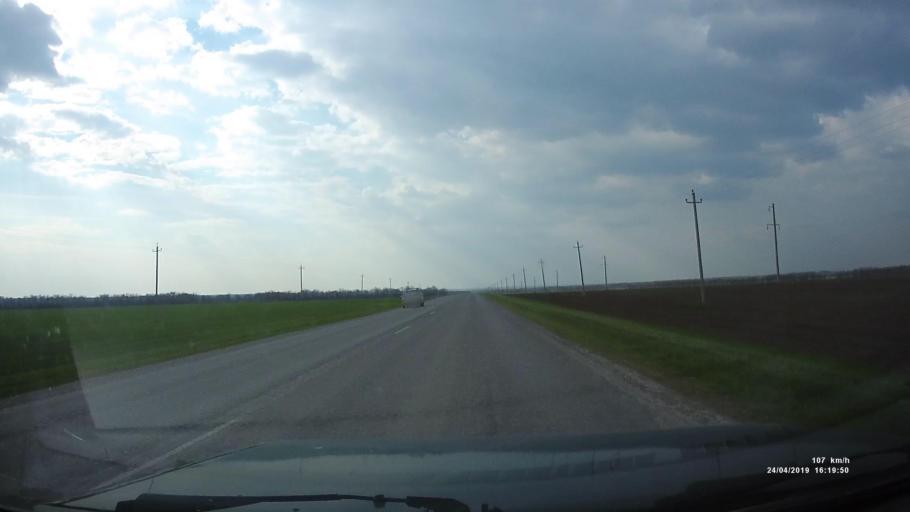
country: RU
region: Rostov
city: Sovetskoye
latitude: 46.7861
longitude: 42.0895
